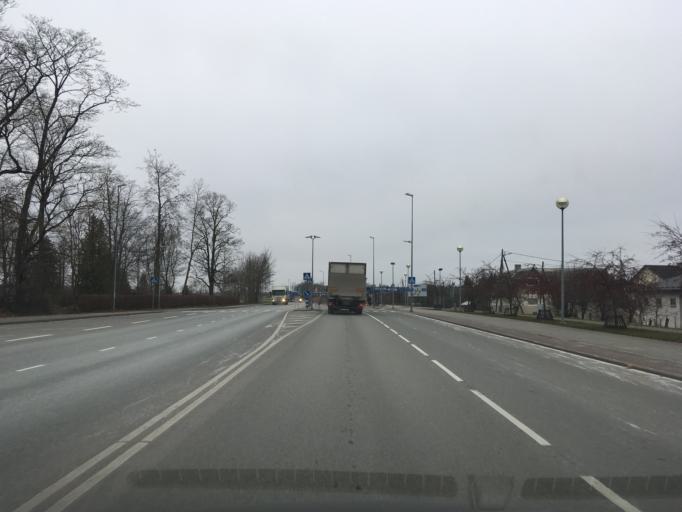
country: EE
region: Ida-Virumaa
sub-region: Johvi vald
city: Johvi
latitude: 59.3652
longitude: 27.3975
